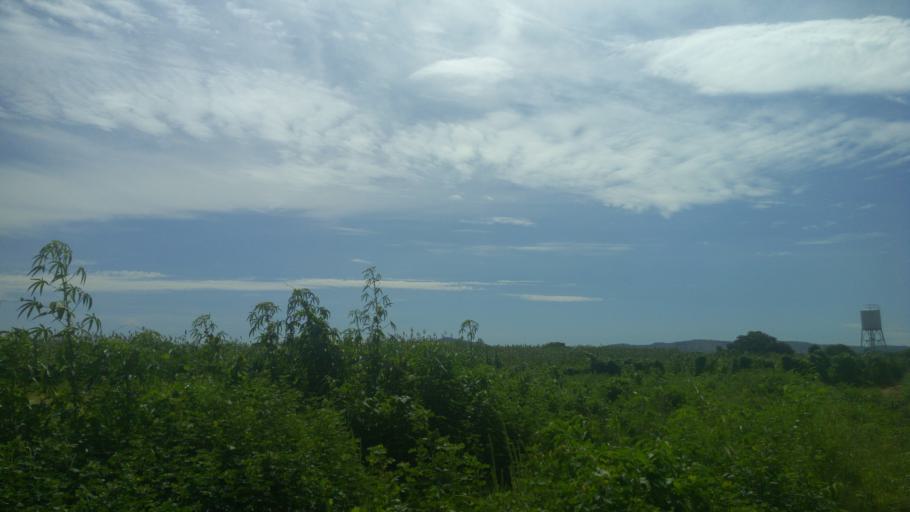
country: ML
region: Kayes
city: Yelimane
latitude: 14.8448
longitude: -10.7471
